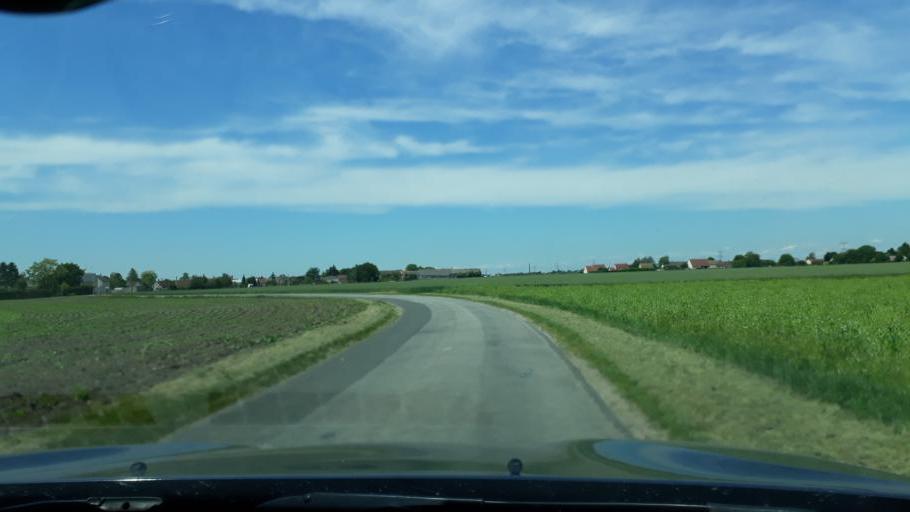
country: FR
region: Centre
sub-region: Departement du Loiret
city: Dadonville
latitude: 48.1020
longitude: 2.2521
